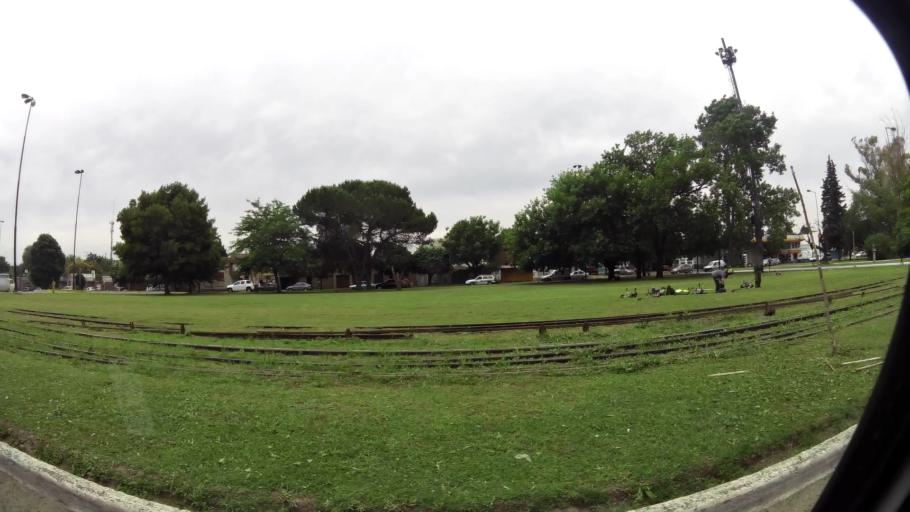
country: AR
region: Buenos Aires
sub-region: Partido de La Plata
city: La Plata
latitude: -34.9436
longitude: -57.9671
